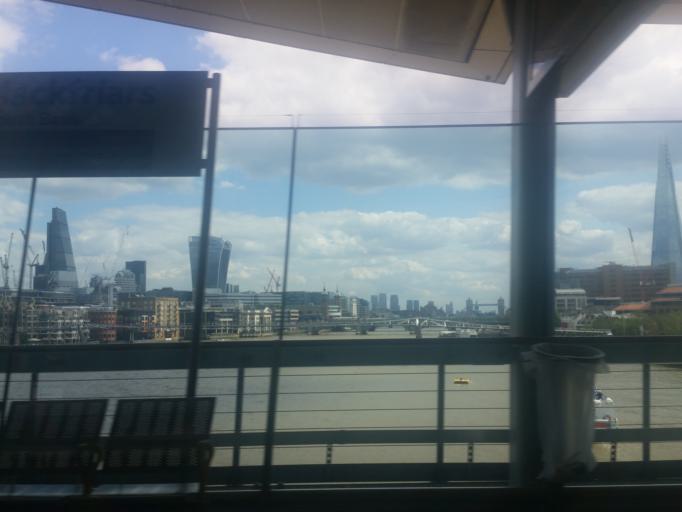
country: GB
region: England
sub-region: Greater London
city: City of London
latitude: 51.5095
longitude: -0.1031
